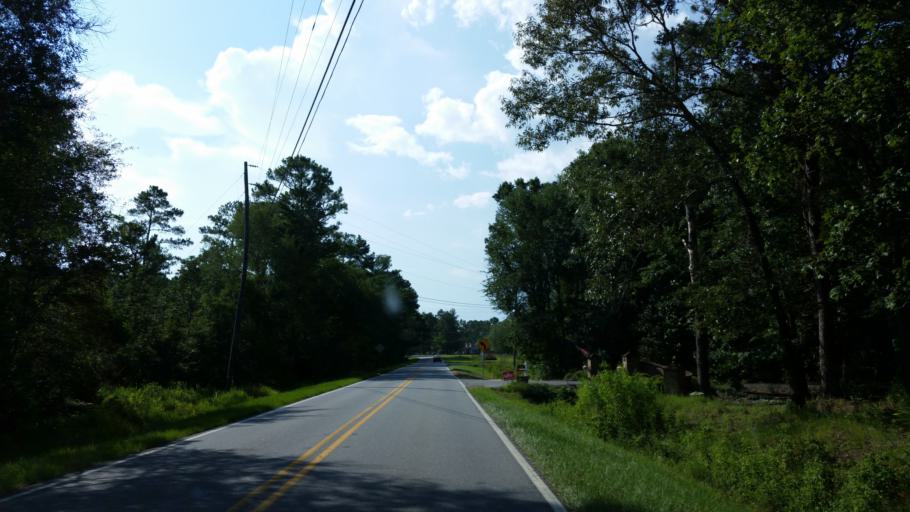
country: US
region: Georgia
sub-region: Lowndes County
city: Remerton
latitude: 30.8958
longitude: -83.3708
